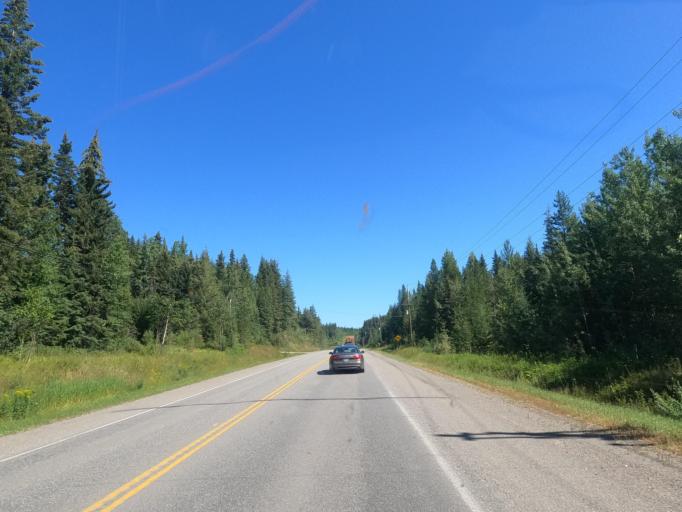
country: CA
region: British Columbia
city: Quesnel
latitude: 53.0530
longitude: -122.4528
